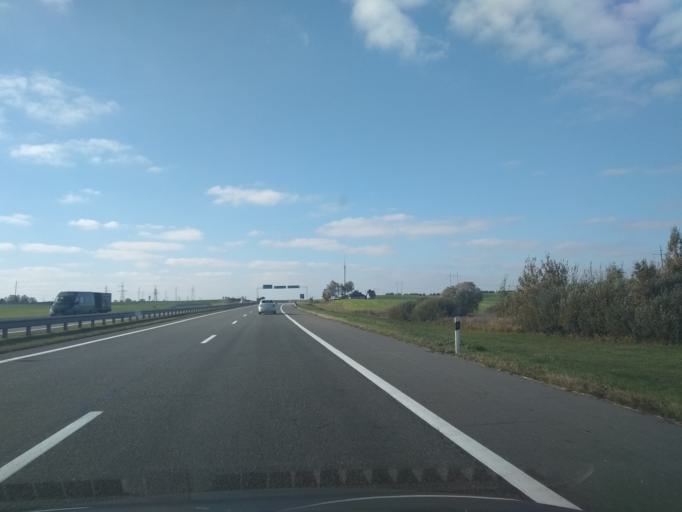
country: BY
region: Brest
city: Baranovichi
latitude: 53.1817
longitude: 26.0466
